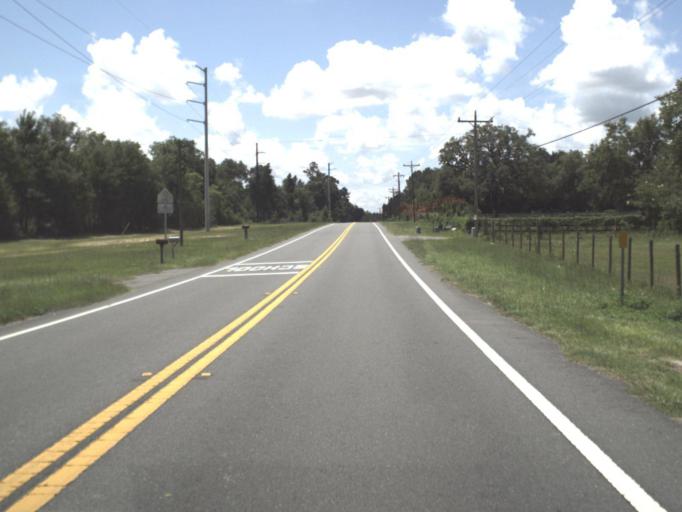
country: US
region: Florida
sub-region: Alachua County
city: Hawthorne
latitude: 29.6268
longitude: -82.0286
